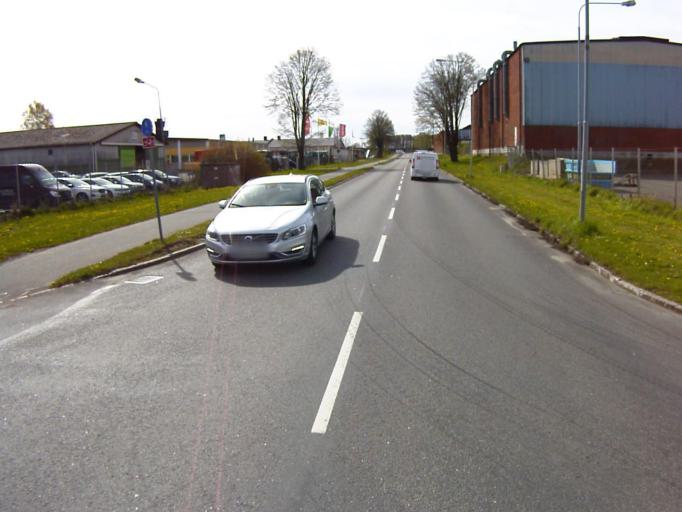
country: SE
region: Skane
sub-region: Kristianstads Kommun
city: Kristianstad
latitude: 56.0162
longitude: 14.1532
